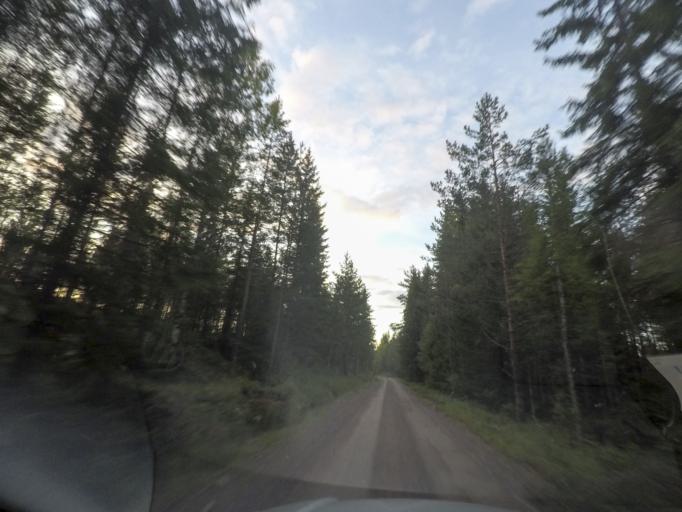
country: SE
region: OErebro
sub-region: Hallefors Kommun
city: Haellefors
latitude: 59.9614
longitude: 14.5395
